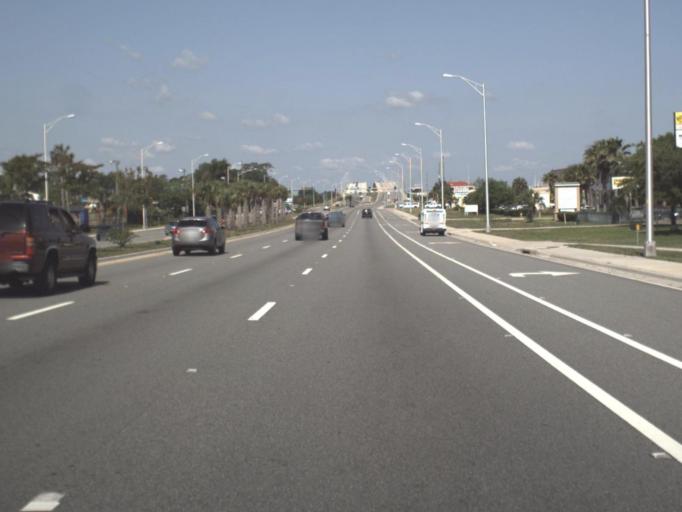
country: US
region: Florida
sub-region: Duval County
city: Jacksonville Beach
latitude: 30.2882
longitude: -81.4097
